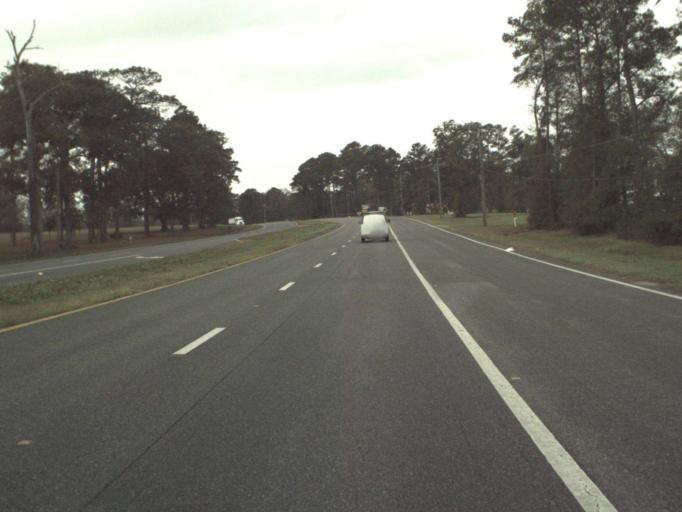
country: US
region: Florida
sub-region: Gadsden County
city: Havana
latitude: 30.6675
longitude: -84.4054
